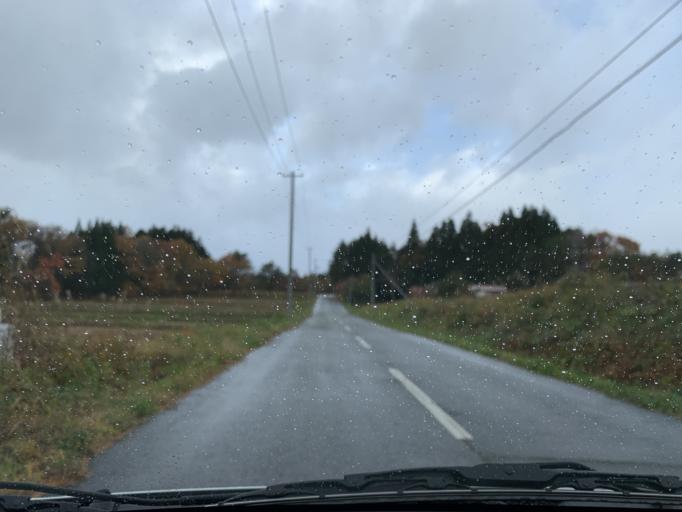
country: JP
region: Iwate
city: Mizusawa
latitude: 39.0972
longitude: 140.9826
